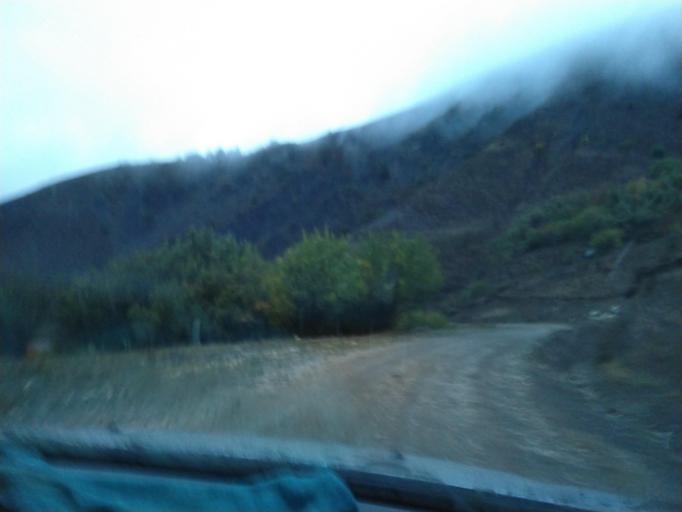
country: RU
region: North Ossetia
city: Tarskoye
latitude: 42.8234
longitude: 44.9702
